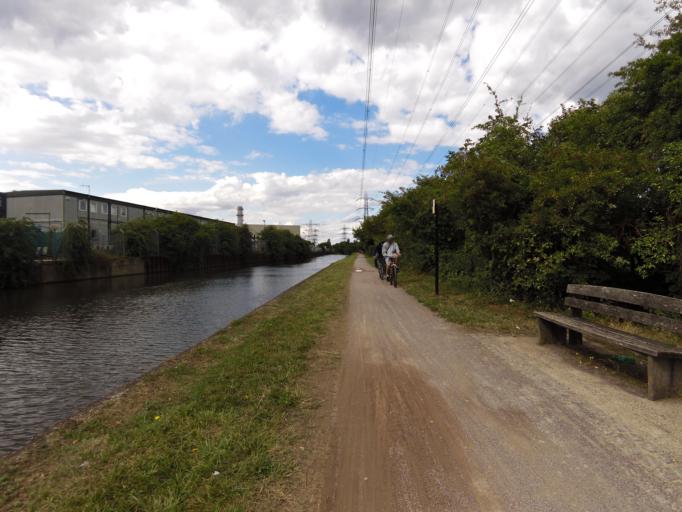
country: GB
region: England
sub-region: Essex
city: Waltham Abbey
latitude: 51.6589
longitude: -0.0203
